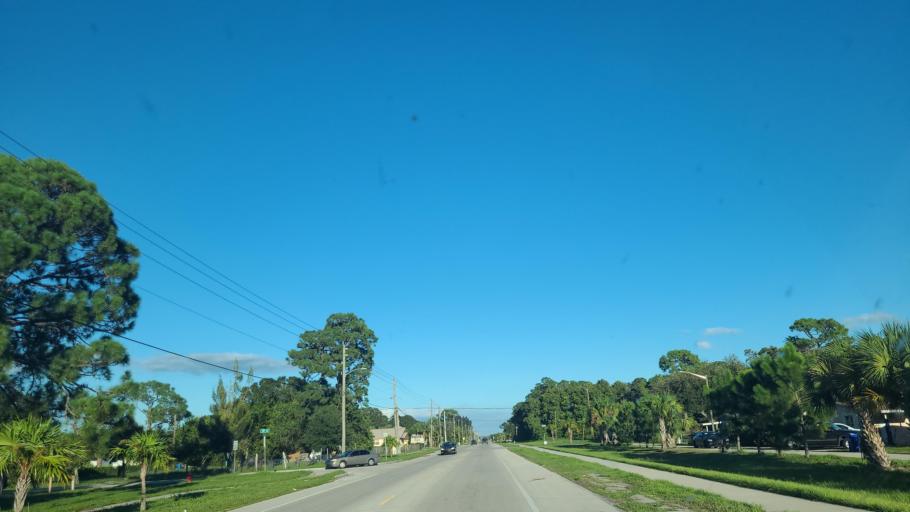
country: US
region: Florida
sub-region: Indian River County
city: Gifford
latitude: 27.6751
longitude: -80.4247
